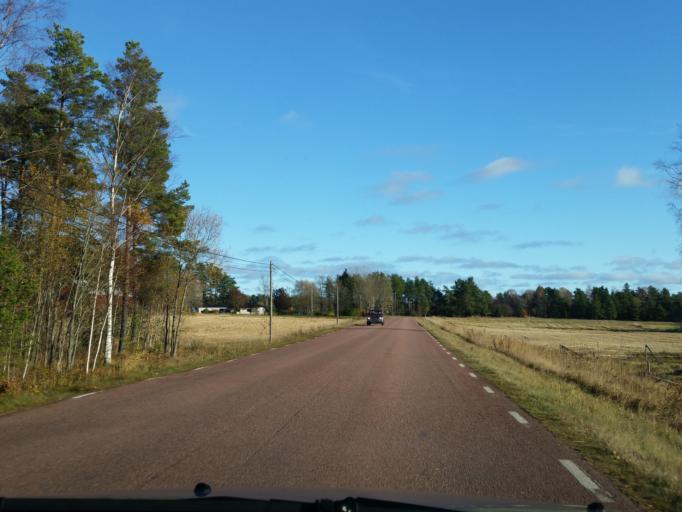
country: AX
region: Alands landsbygd
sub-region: Jomala
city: Jomala
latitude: 60.1581
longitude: 19.9162
